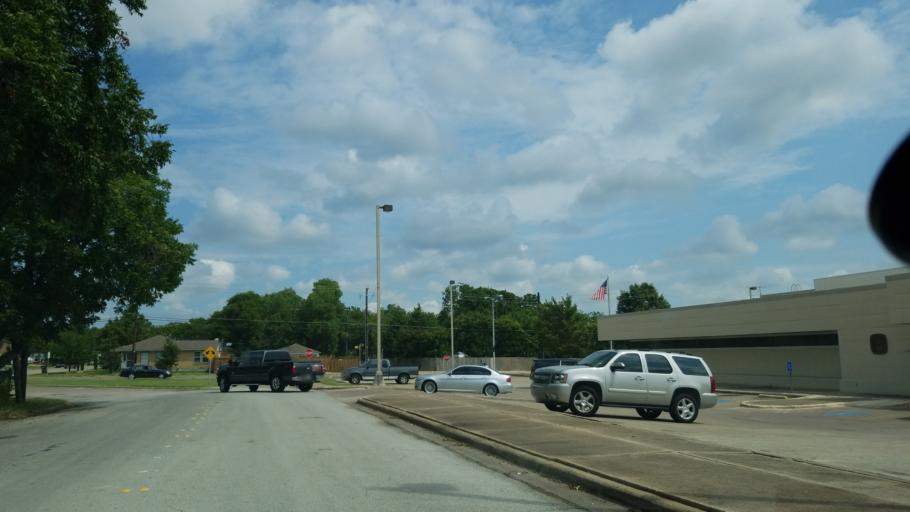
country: US
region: Texas
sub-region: Dallas County
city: Garland
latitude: 32.9154
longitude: -96.6441
